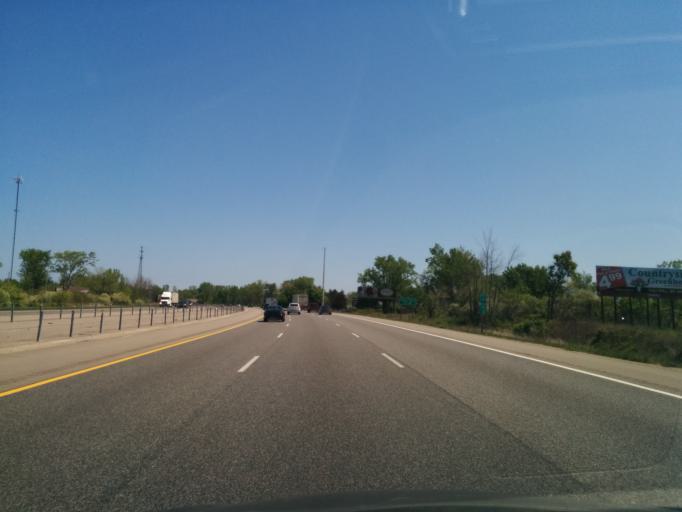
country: US
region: Michigan
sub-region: Berrien County
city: Bridgman
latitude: 41.9191
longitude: -86.5723
